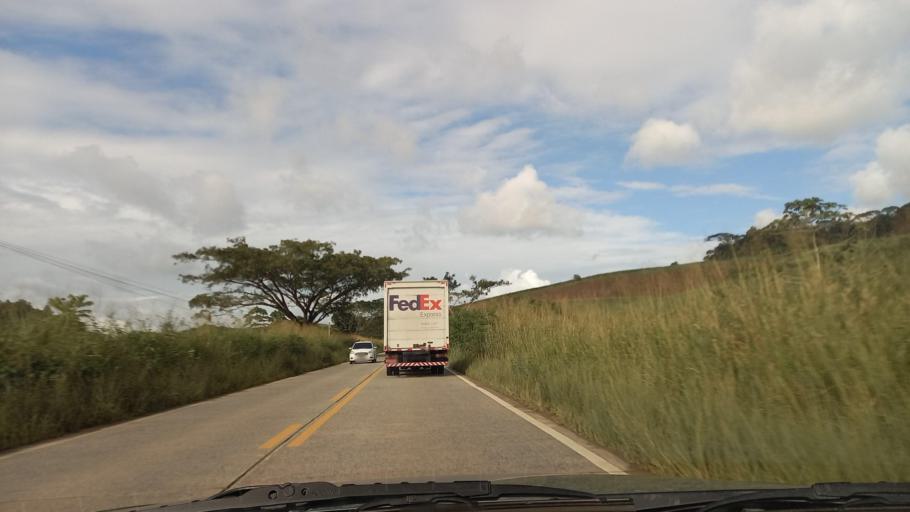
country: BR
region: Pernambuco
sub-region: Catende
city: Catende
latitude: -8.6953
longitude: -35.6915
